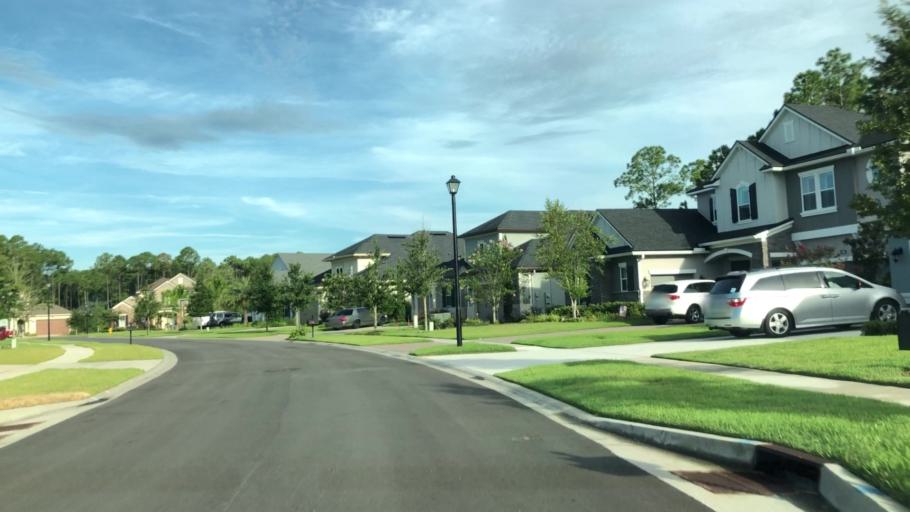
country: US
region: Florida
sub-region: Saint Johns County
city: Palm Valley
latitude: 30.1336
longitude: -81.4271
